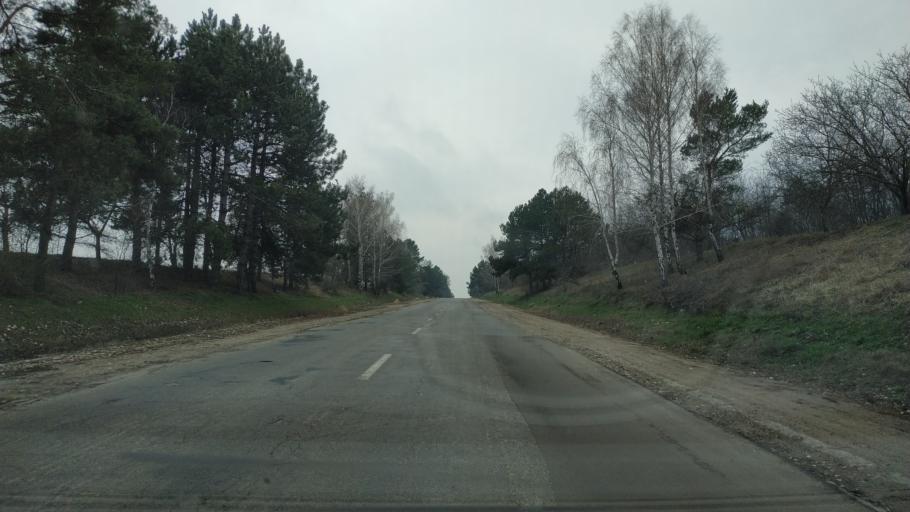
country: MD
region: Cahul
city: Cahul
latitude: 45.9405
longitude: 28.2919
